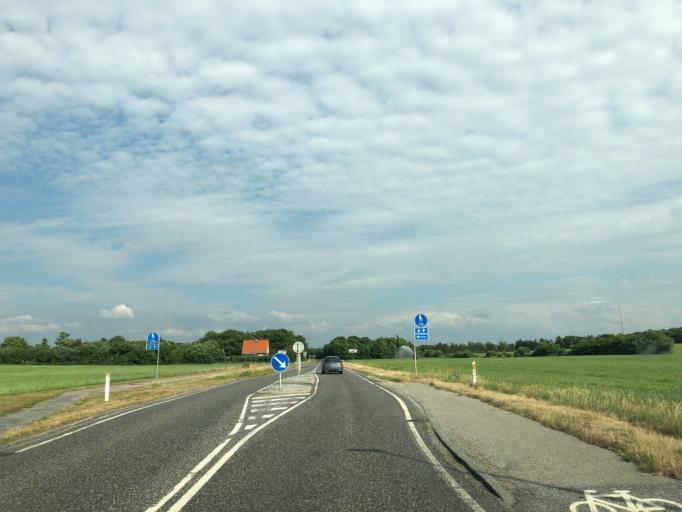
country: DK
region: Central Jutland
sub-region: Ringkobing-Skjern Kommune
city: Skjern
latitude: 55.9017
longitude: 8.4541
